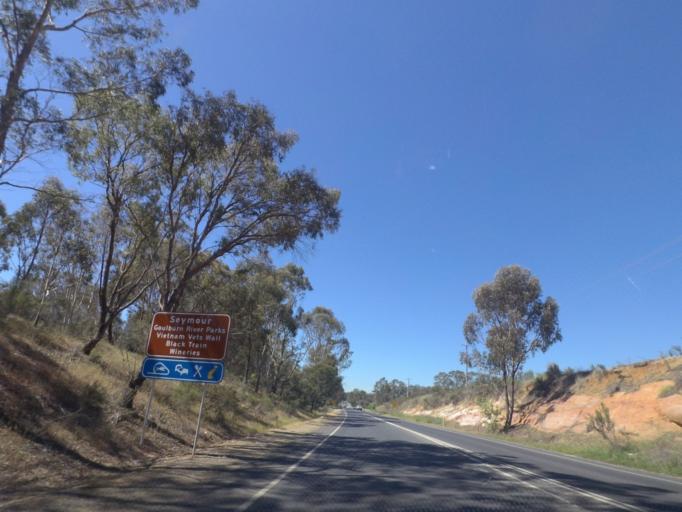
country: AU
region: Victoria
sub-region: Murrindindi
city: Kinglake West
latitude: -37.0290
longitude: 145.1062
